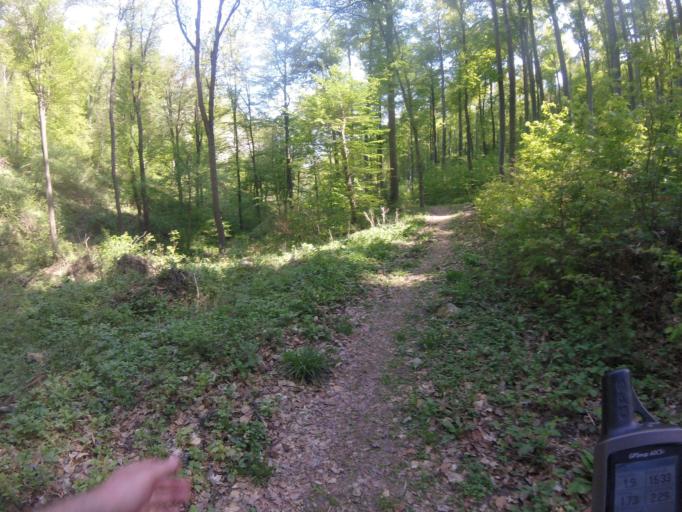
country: HU
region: Pest
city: Pilisszentkereszt
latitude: 47.7104
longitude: 18.8930
